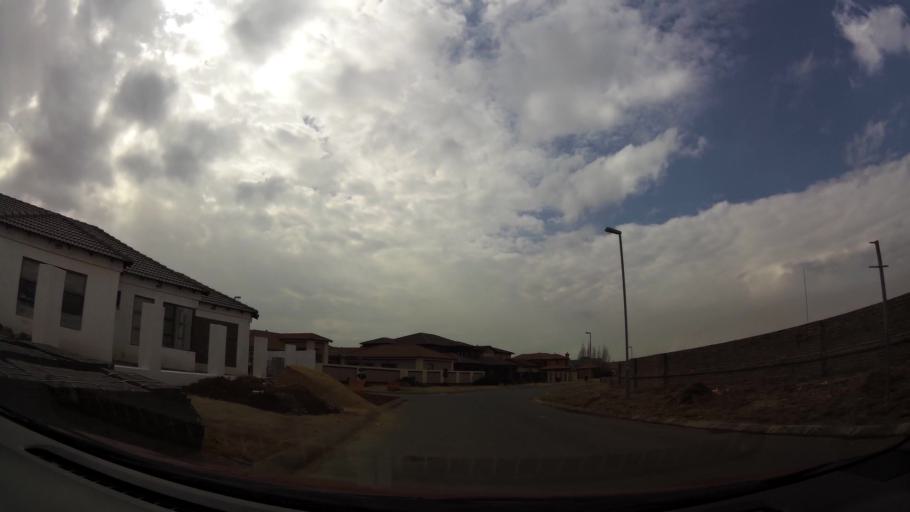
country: ZA
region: Gauteng
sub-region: Sedibeng District Municipality
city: Vanderbijlpark
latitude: -26.7242
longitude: 27.8651
